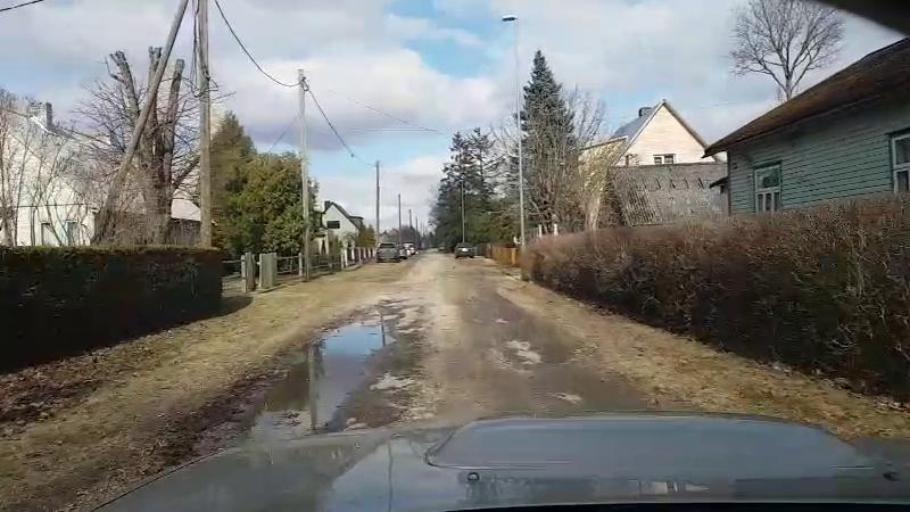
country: EE
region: Jaervamaa
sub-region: Paide linn
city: Paide
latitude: 58.8819
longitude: 25.5419
